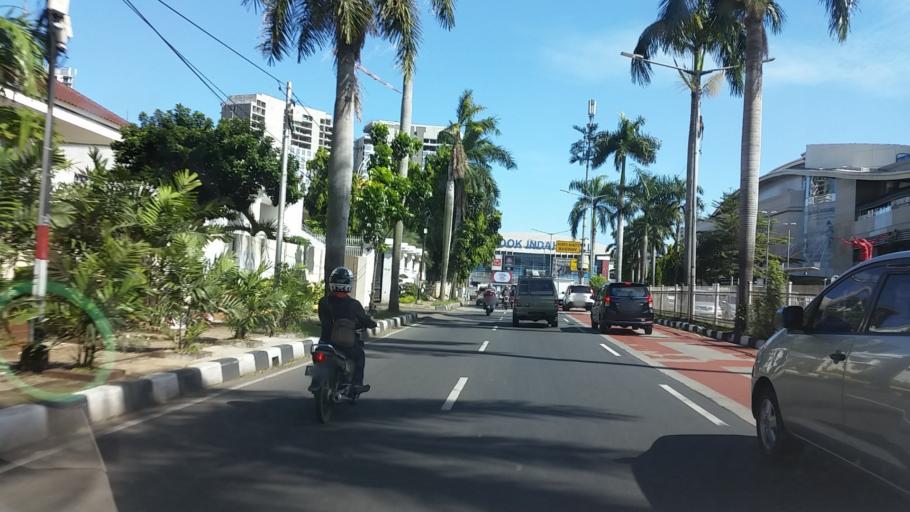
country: ID
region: Banten
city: South Tangerang
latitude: -6.2687
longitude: 106.7836
